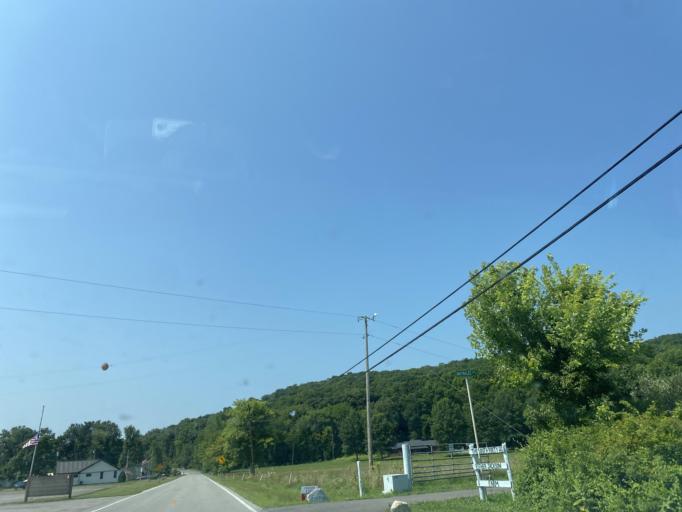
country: US
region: Kentucky
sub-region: Campbell County
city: Claryville
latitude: 38.8649
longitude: -84.4595
